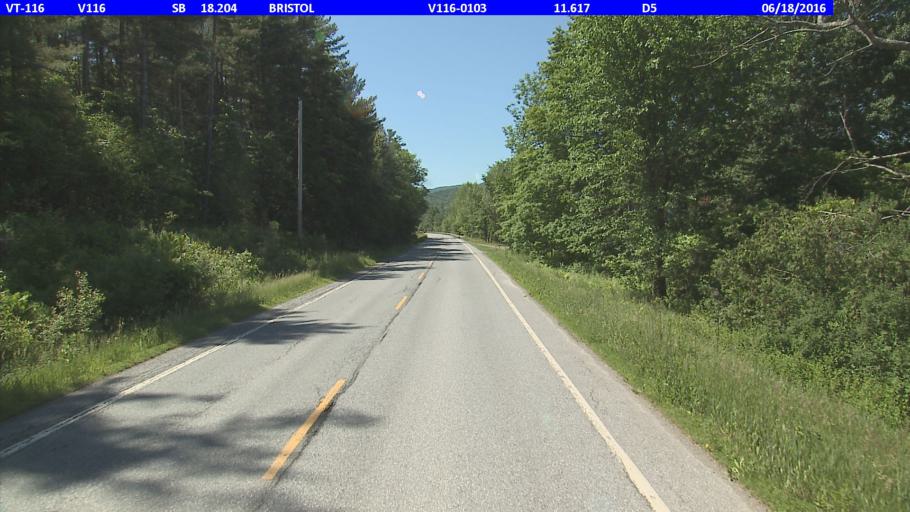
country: US
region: Vermont
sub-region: Addison County
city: Bristol
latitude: 44.1766
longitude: -73.0571
